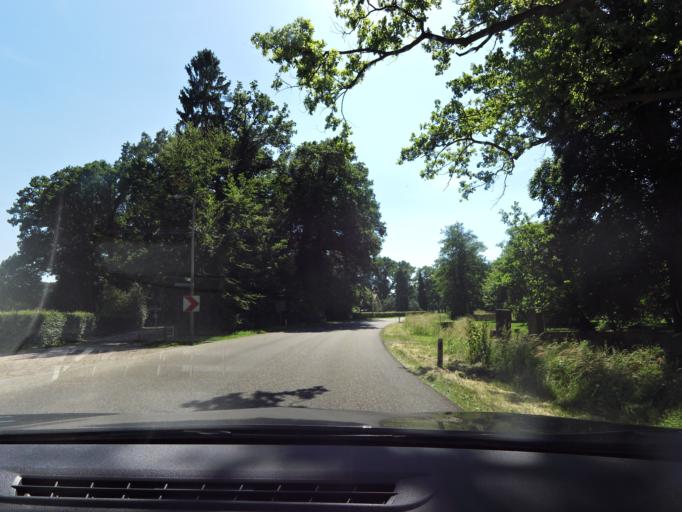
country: NL
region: Overijssel
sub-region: Gemeente Hof van Twente
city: Goor
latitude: 52.2160
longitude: 6.5789
